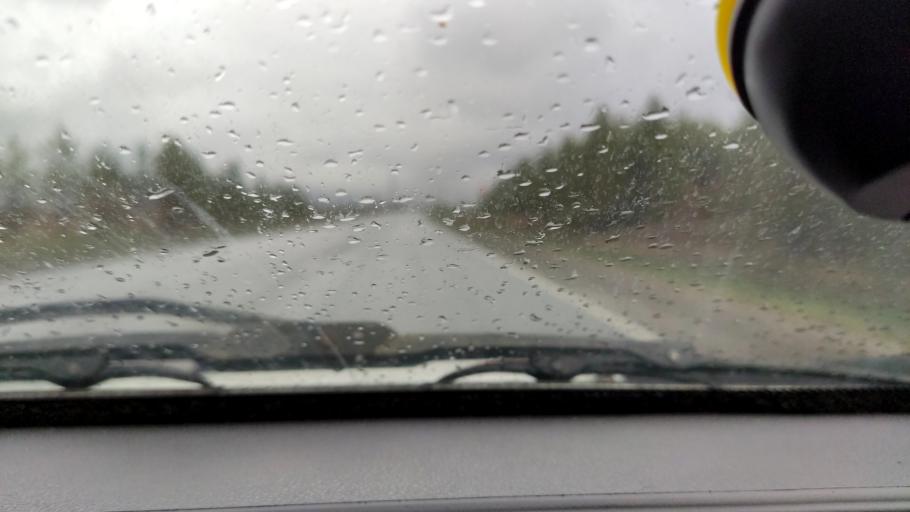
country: RU
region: Samara
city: Zhigulevsk
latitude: 53.5731
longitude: 49.5542
